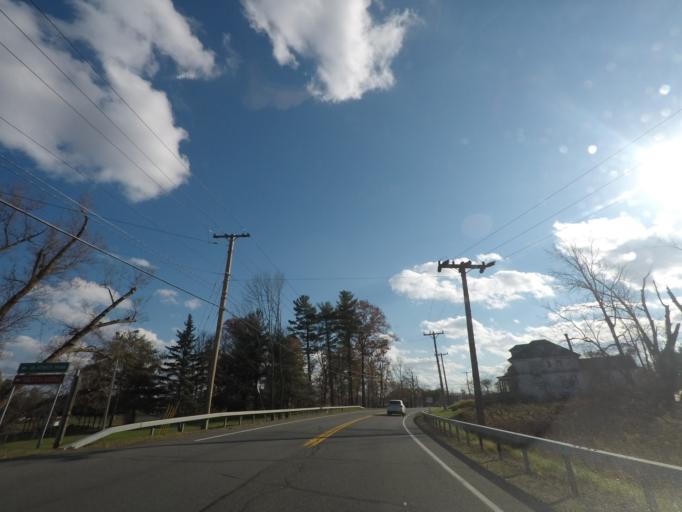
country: US
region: New York
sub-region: Schenectady County
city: Niskayuna
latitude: 42.8154
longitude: -73.8660
